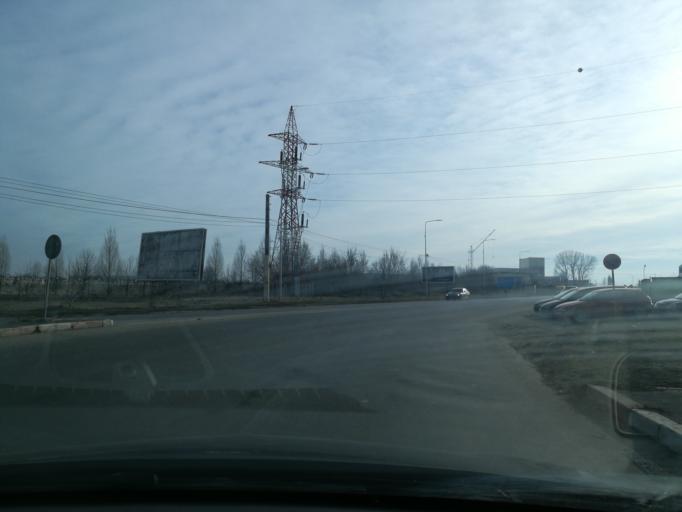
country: RO
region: Constanta
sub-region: Municipiul Constanta
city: Palazu Mare
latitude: 44.1963
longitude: 28.6042
